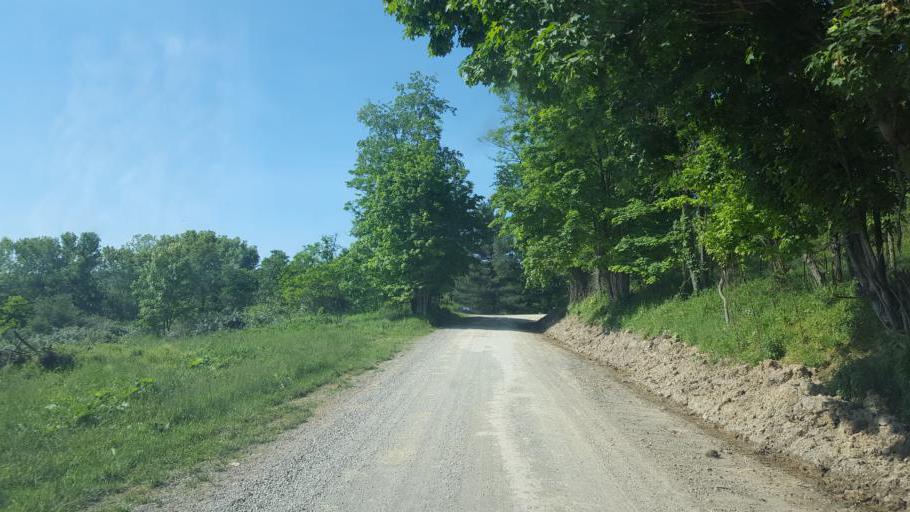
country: US
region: Ohio
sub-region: Jackson County
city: Wellston
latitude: 38.9940
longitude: -82.4181
